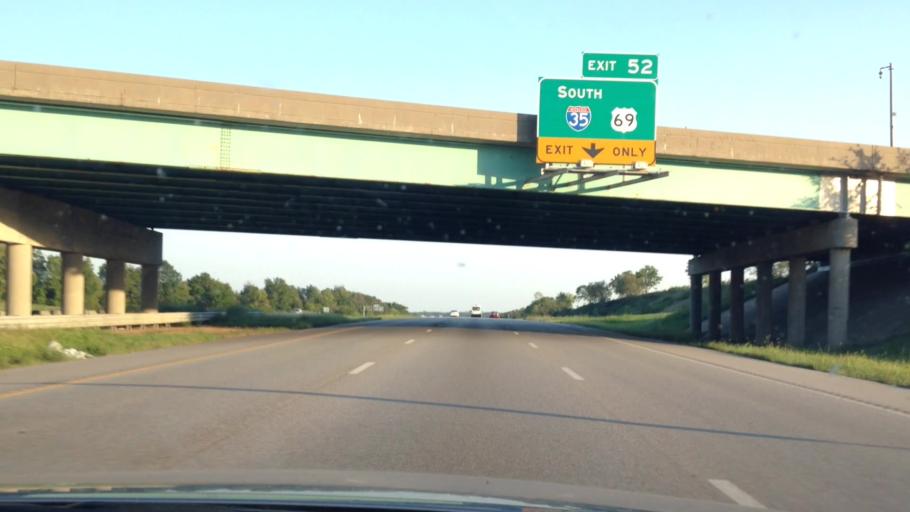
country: US
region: Missouri
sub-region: Clay County
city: Pleasant Valley
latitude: 39.2247
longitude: -94.5000
